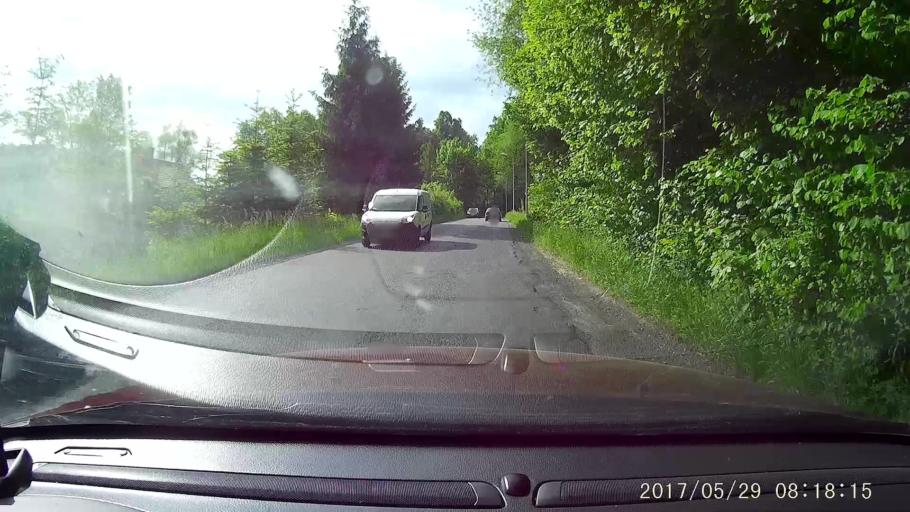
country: PL
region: Lower Silesian Voivodeship
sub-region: Powiat zlotoryjski
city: Zlotoryja
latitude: 51.1095
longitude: 15.8914
